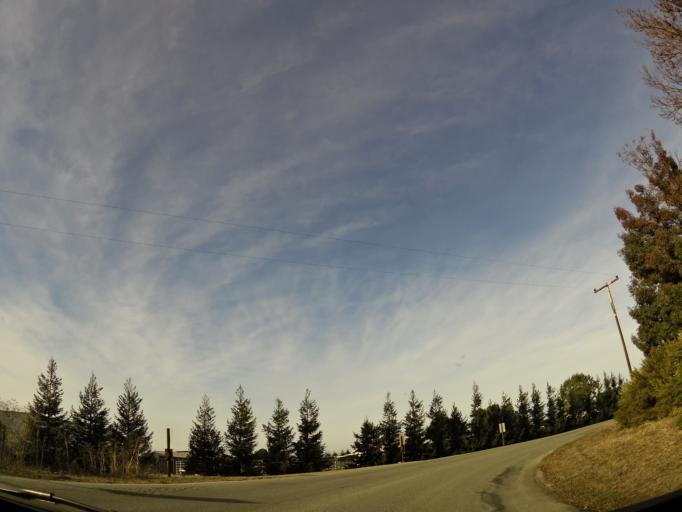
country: US
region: California
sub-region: San Benito County
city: Hollister
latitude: 36.8172
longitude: -121.4041
